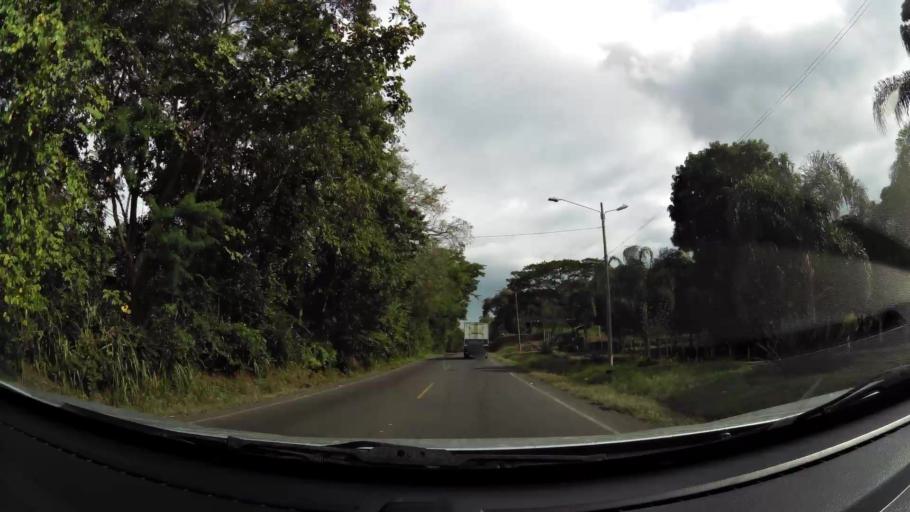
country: CR
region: Guanacaste
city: Juntas
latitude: 10.1753
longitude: -84.9278
